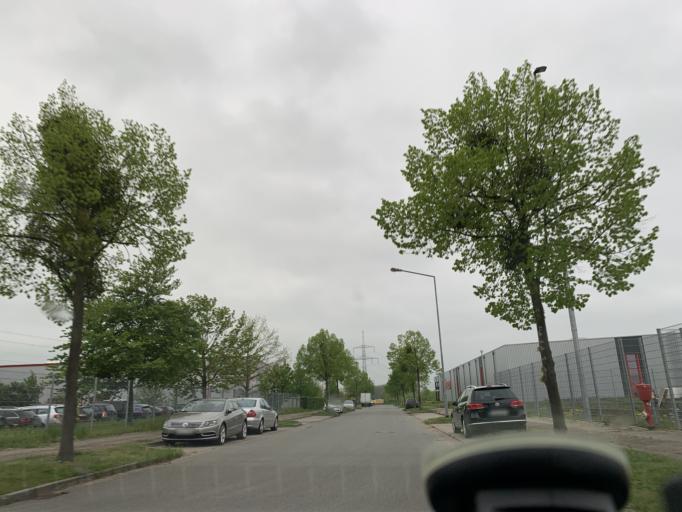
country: DE
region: Brandenburg
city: Nauen
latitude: 52.5968
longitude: 12.8925
